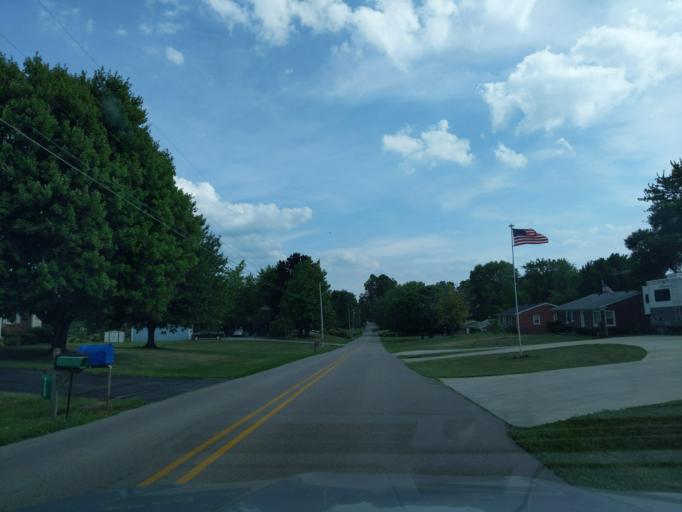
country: US
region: Indiana
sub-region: Decatur County
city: Greensburg
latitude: 39.3258
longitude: -85.4703
